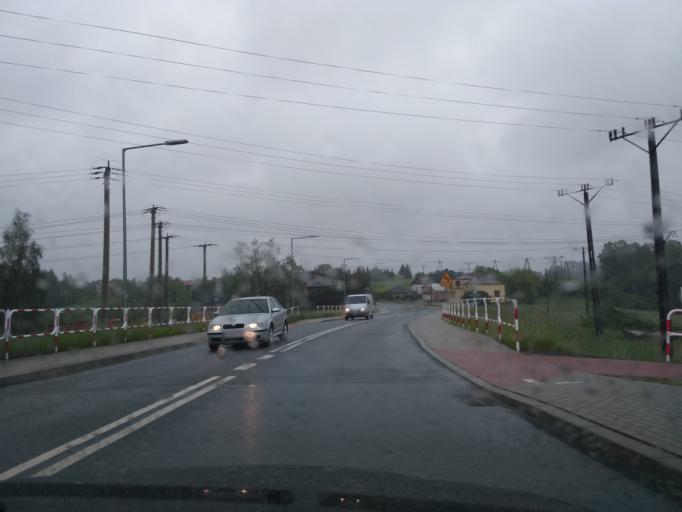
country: PL
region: Lesser Poland Voivodeship
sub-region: Powiat gorlicki
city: Gorlice
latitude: 49.6741
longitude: 21.1410
